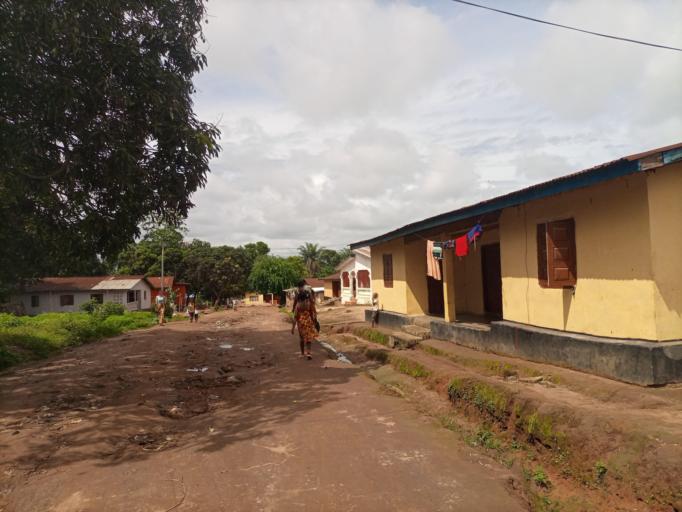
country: SL
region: Northern Province
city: Masoyila
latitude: 8.6021
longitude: -13.1797
